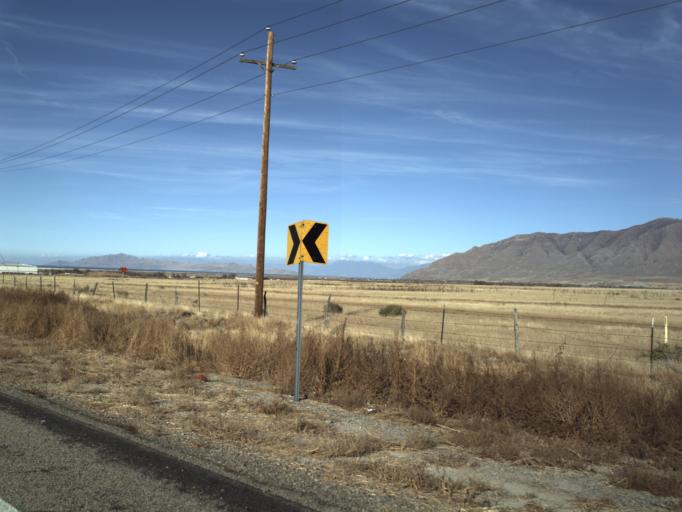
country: US
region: Utah
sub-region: Tooele County
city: Erda
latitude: 40.5773
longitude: -112.3675
